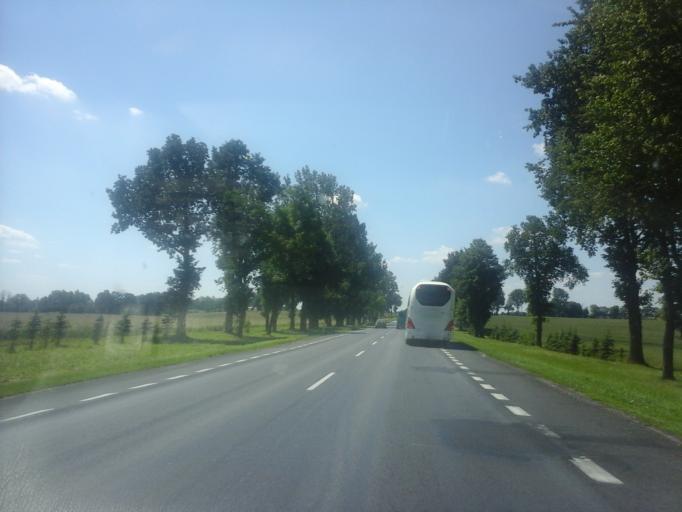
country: PL
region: West Pomeranian Voivodeship
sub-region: Koszalin
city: Koszalin
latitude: 54.1477
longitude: 16.0711
